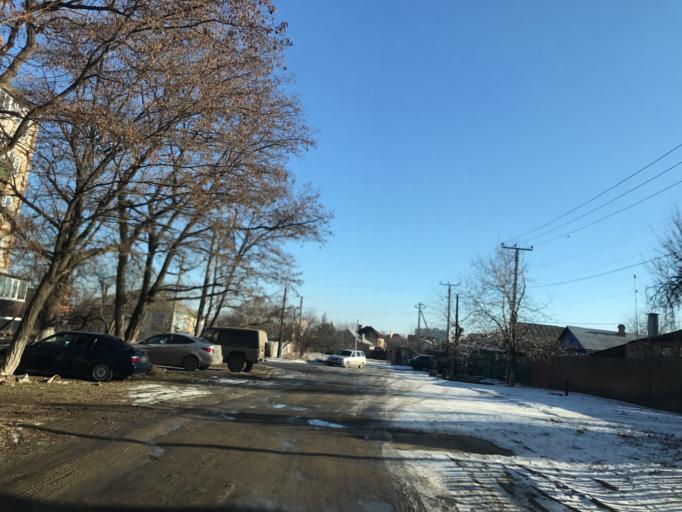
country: RU
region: Rostov
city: Kamensk-Shakhtinskiy
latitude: 48.3133
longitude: 40.2780
